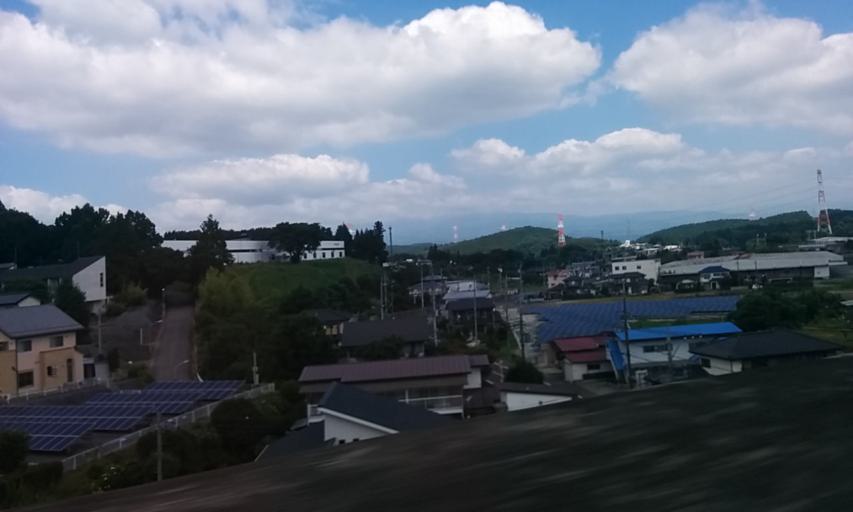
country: JP
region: Tochigi
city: Yaita
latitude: 36.7573
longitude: 139.9420
